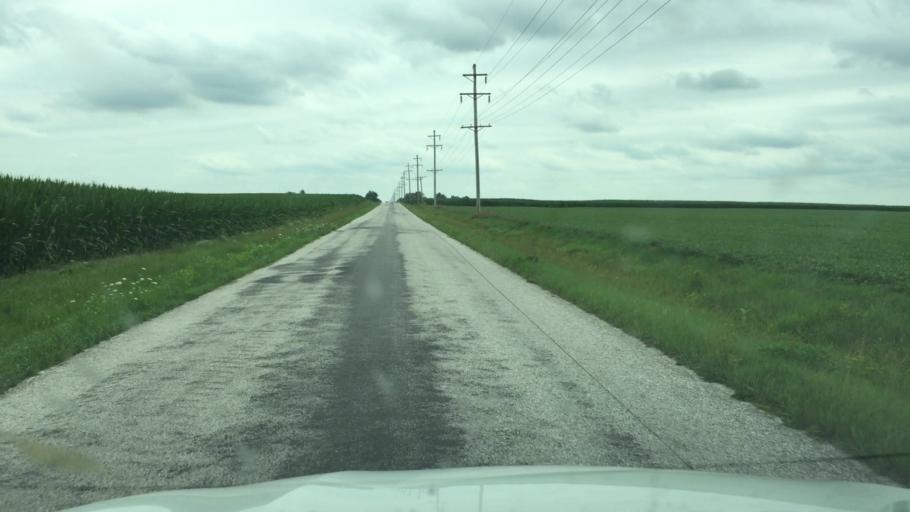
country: US
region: Illinois
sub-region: Hancock County
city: Carthage
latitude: 40.3399
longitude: -91.0823
